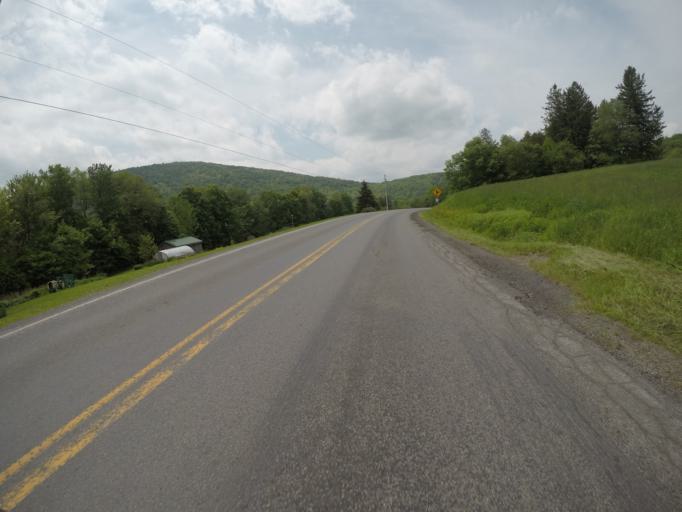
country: US
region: New York
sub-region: Delaware County
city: Delhi
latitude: 42.2595
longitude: -74.7684
